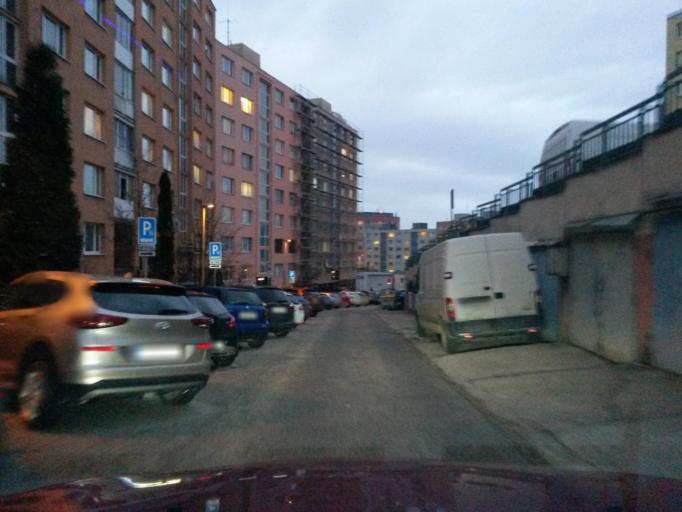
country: SK
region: Kosicky
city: Kosice
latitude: 48.7313
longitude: 21.2834
